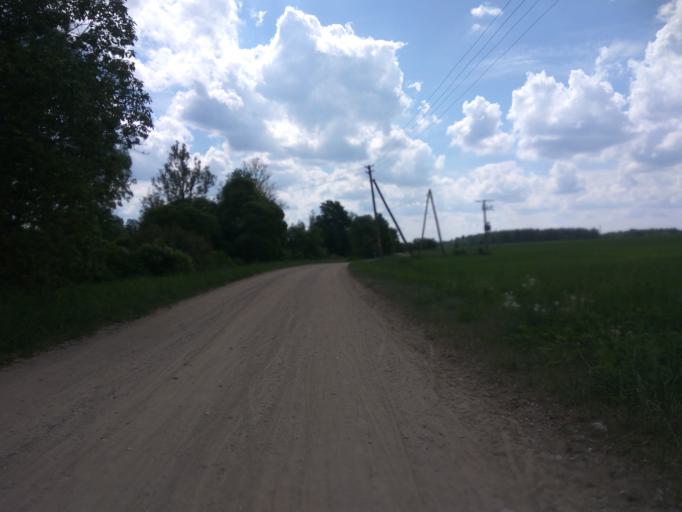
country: LV
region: Kuldigas Rajons
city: Kuldiga
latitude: 56.8918
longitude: 21.9706
